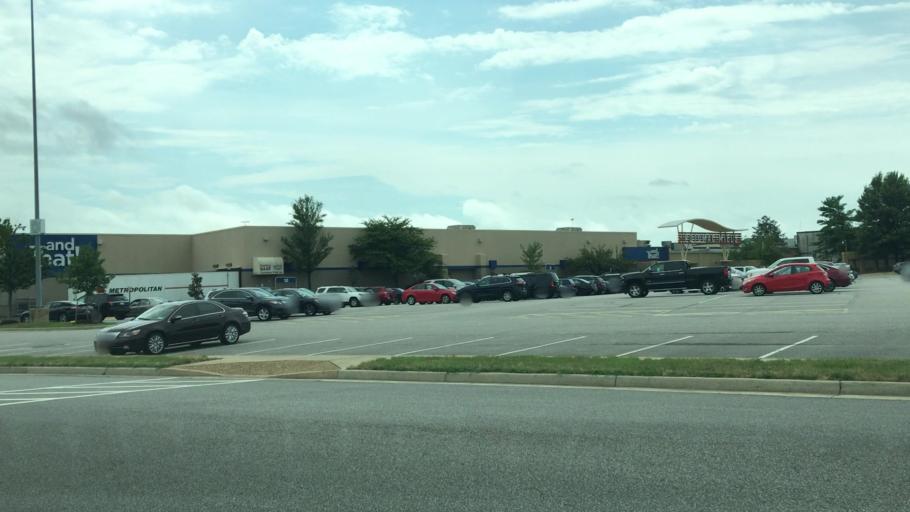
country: US
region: Virginia
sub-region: Prince William County
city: Potomac Mills
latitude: 38.6463
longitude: -77.2944
